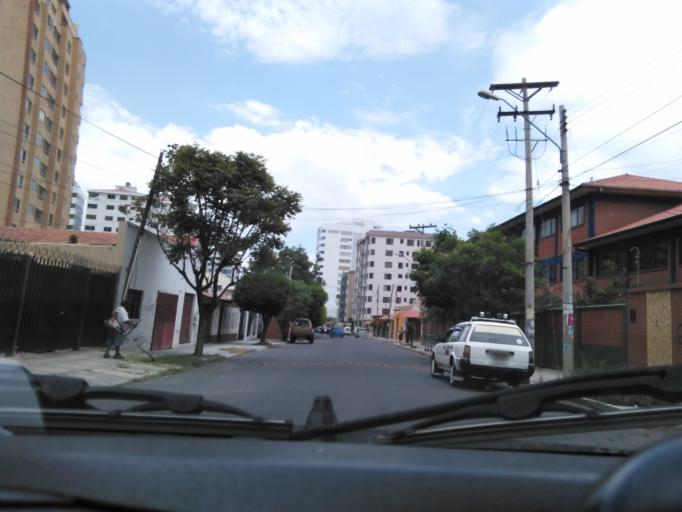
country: BO
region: Cochabamba
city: Cochabamba
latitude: -17.3700
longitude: -66.1641
